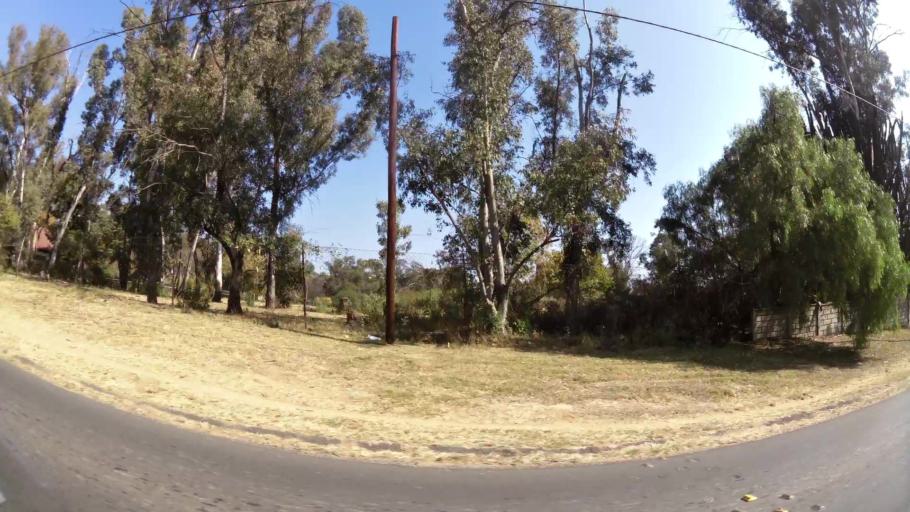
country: ZA
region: Gauteng
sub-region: City of Johannesburg Metropolitan Municipality
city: Modderfontein
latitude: -26.0949
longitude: 28.1324
